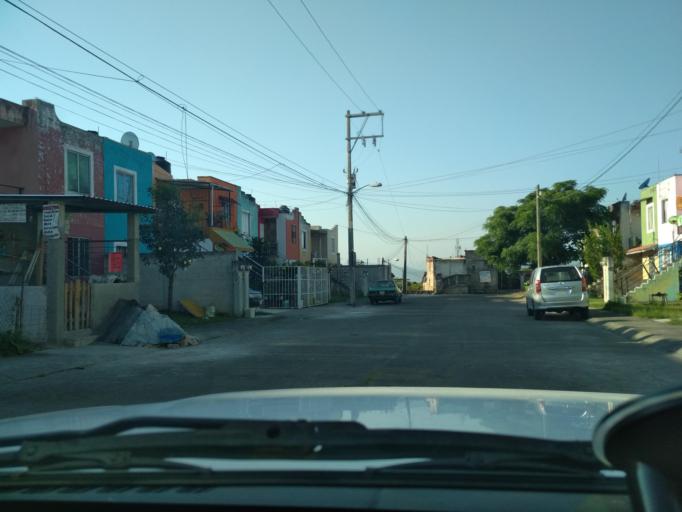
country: MX
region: Veracruz
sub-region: Fortin
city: Fraccionamiento Villas de la Llave
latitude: 18.9178
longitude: -96.9939
